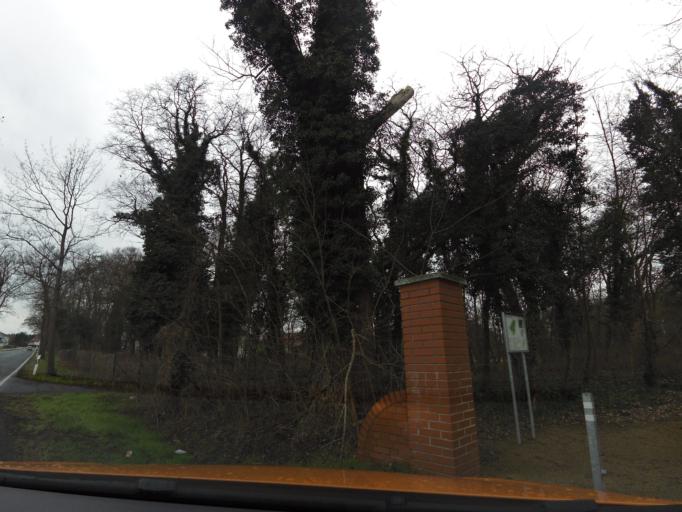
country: DE
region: Brandenburg
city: Rangsdorf
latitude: 52.3213
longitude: 13.4460
